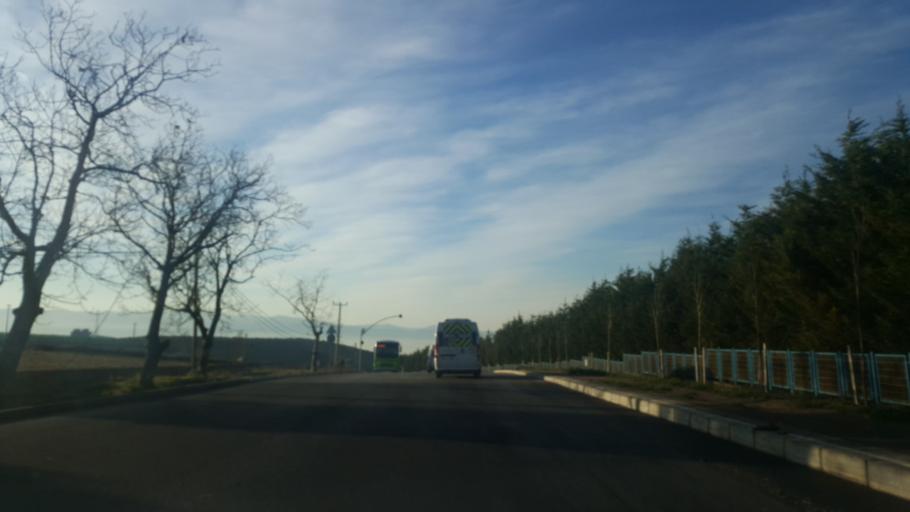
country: TR
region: Kocaeli
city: Tavsancil
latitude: 40.8006
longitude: 29.5518
